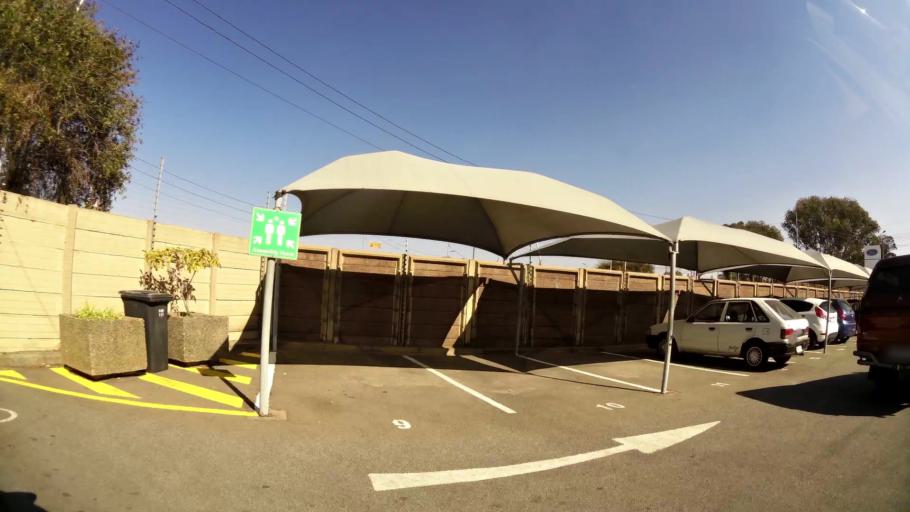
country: ZA
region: Gauteng
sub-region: City of Johannesburg Metropolitan Municipality
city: Johannesburg
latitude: -26.2144
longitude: 28.0309
